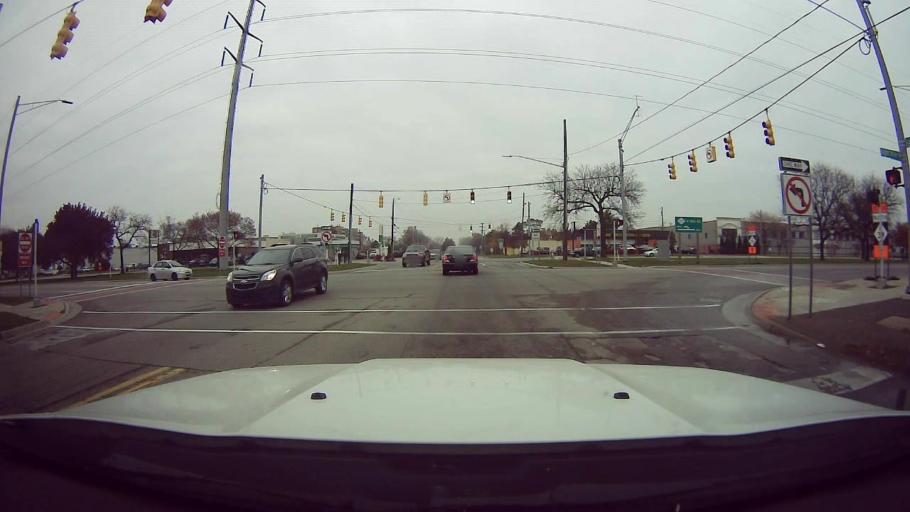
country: US
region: Michigan
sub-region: Oakland County
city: Southfield
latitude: 42.4431
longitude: -83.2588
